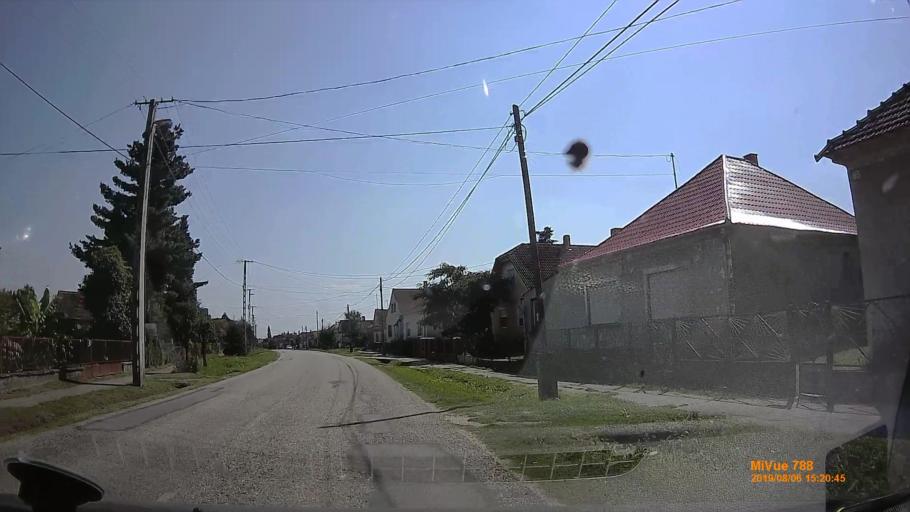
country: HR
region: Koprivnicko-Krizevacka
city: Drnje
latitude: 46.2815
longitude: 16.9473
